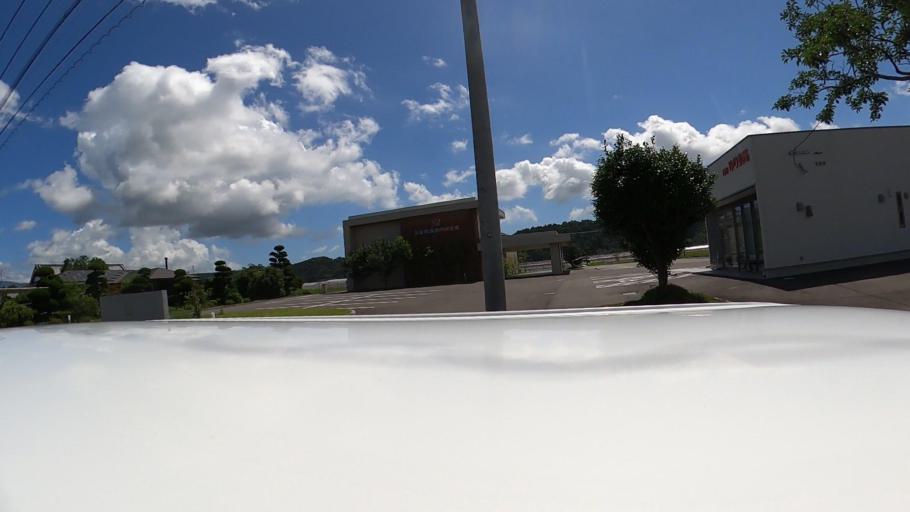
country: JP
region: Miyazaki
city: Tsuma
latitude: 32.0985
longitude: 131.4090
